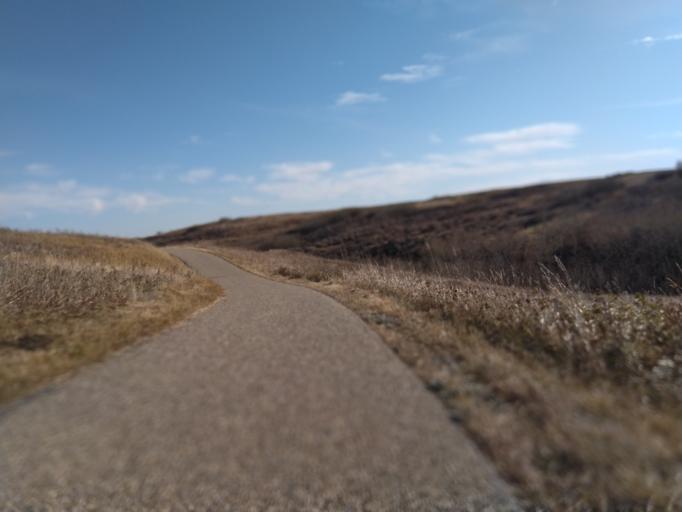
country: CA
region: Alberta
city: Calgary
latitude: 51.1207
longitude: -114.1102
